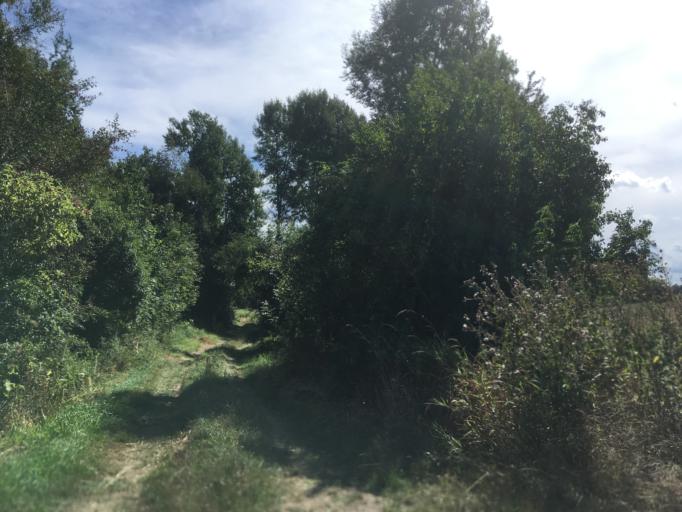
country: DE
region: Brandenburg
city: Gerswalde
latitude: 53.1306
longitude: 13.7858
